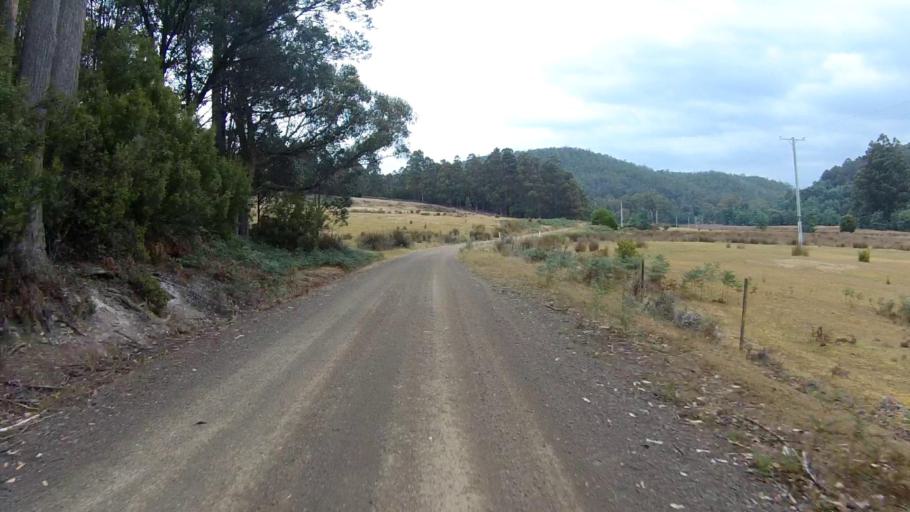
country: AU
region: Tasmania
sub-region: Kingborough
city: Kettering
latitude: -43.2163
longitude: 147.1770
